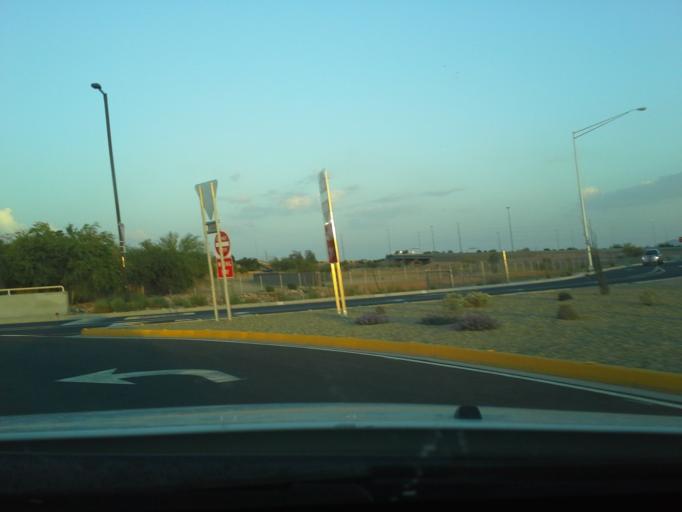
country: US
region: Arizona
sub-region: Maricopa County
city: Paradise Valley
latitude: 33.6762
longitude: -112.0053
